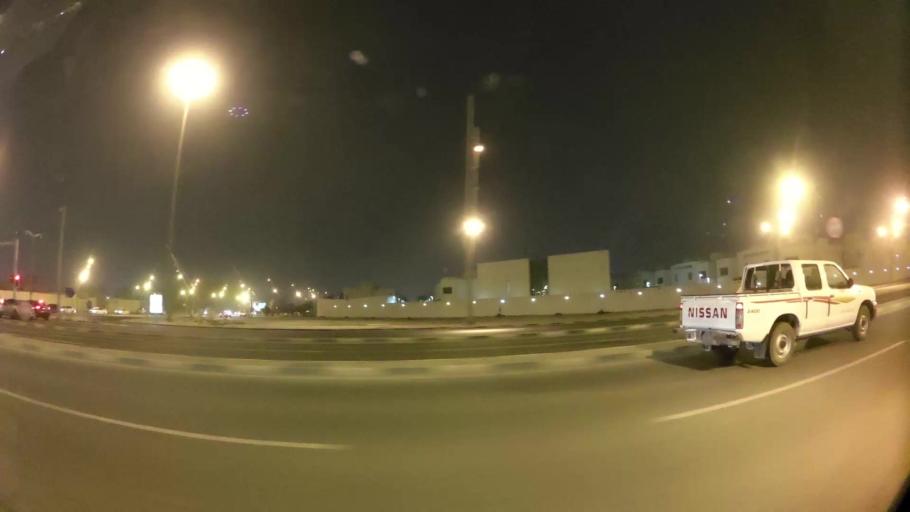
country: QA
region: Baladiyat ar Rayyan
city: Ar Rayyan
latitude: 25.2647
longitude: 51.4632
